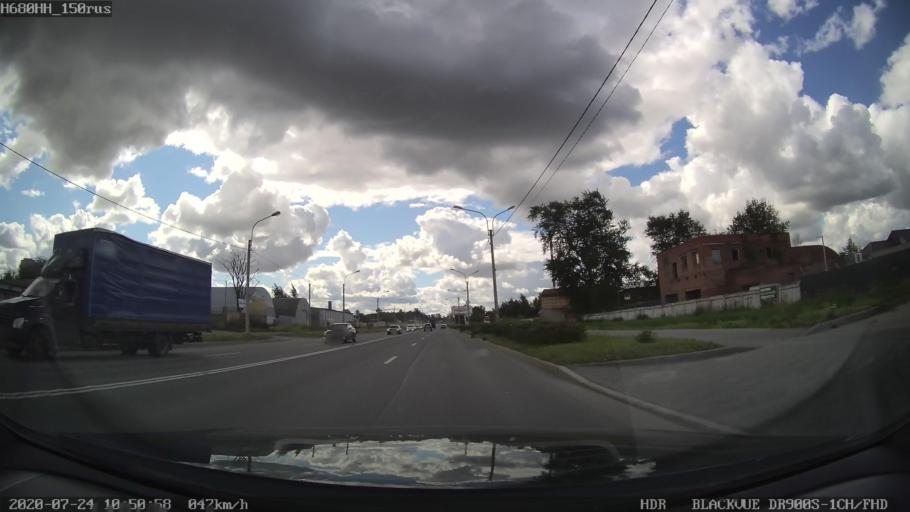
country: RU
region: St.-Petersburg
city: Admiralteisky
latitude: 59.8948
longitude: 30.3006
